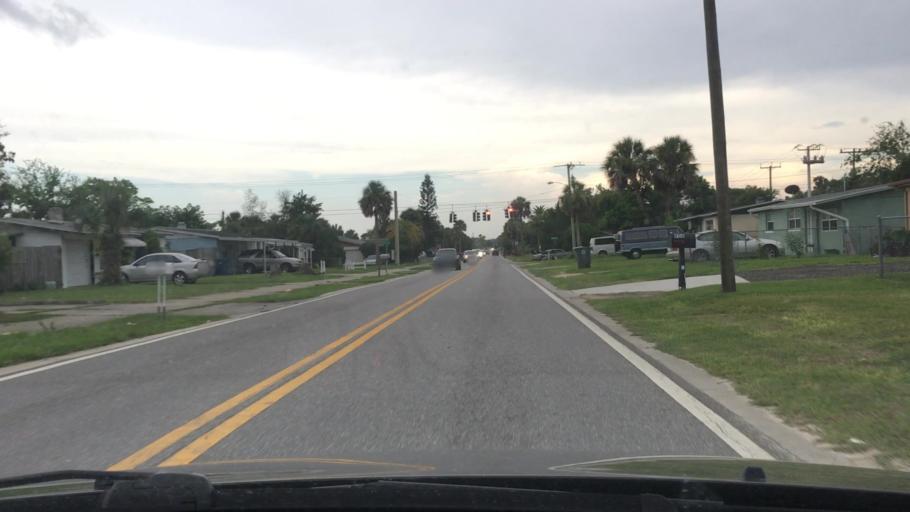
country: US
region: Florida
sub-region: Volusia County
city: Holly Hill
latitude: 29.2265
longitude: -81.0613
